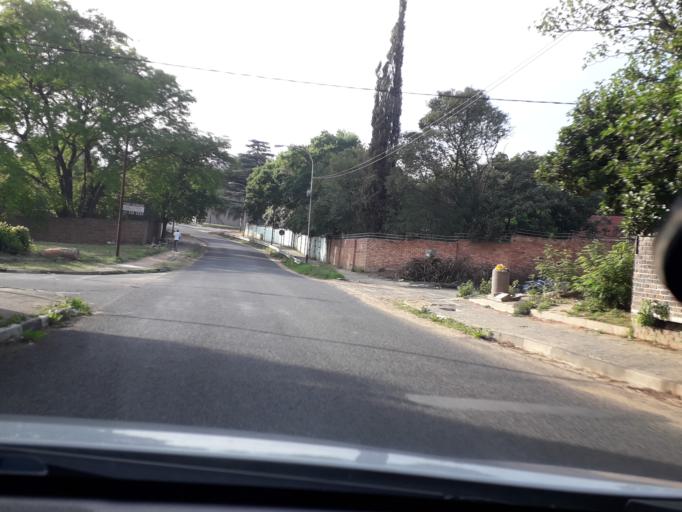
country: ZA
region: Gauteng
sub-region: City of Johannesburg Metropolitan Municipality
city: Modderfontein
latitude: -26.1300
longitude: 28.1043
